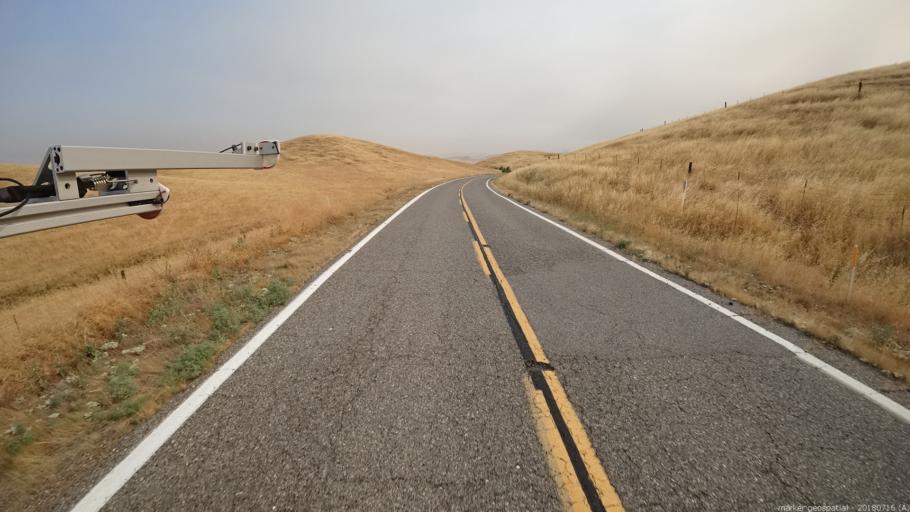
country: US
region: California
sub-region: Madera County
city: Madera Acres
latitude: 37.1853
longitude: -120.0027
